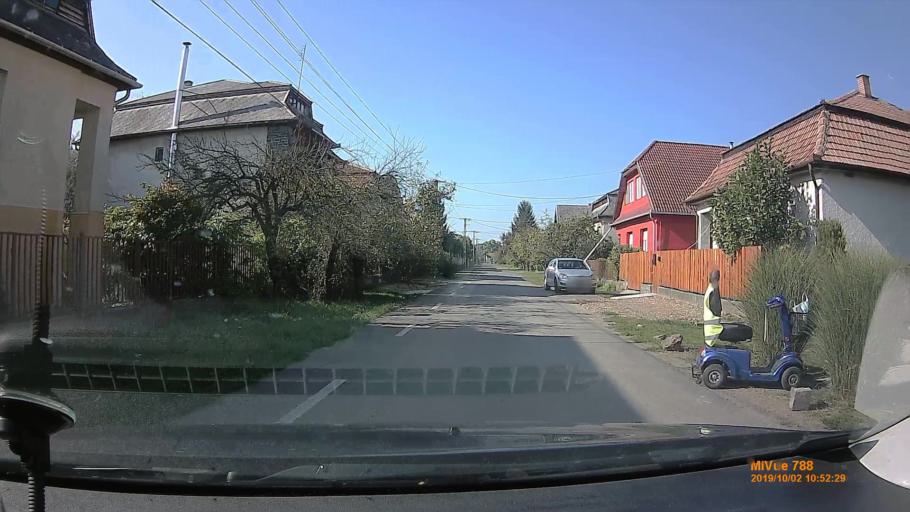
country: HU
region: Nograd
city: Matraverebely
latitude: 47.9737
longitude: 19.7839
